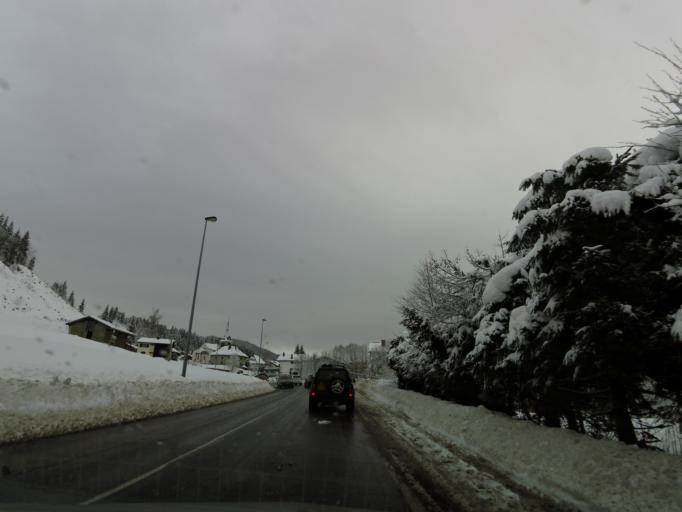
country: FR
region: Rhone-Alpes
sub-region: Departement de la Haute-Savoie
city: Les Gets
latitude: 46.1630
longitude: 6.6737
